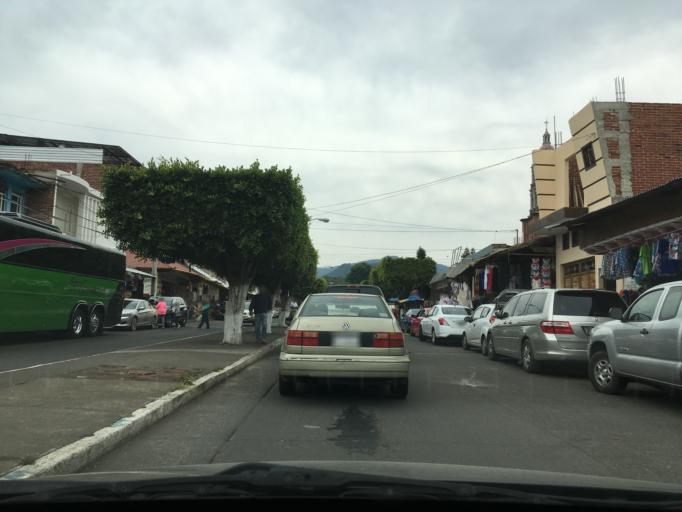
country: MX
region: Michoacan
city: Nuevo San Juan Parangaricutiro
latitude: 19.4160
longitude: -102.1274
